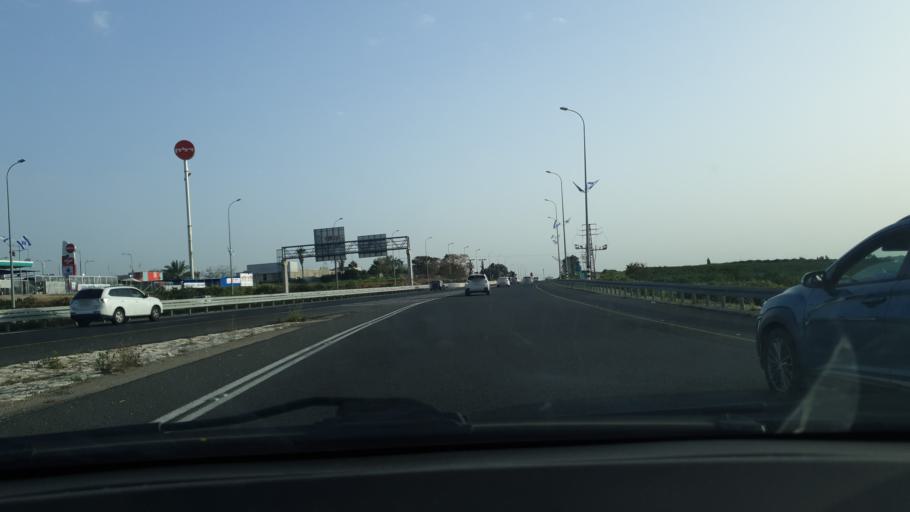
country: IL
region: Central District
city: Even Yehuda
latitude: 32.2522
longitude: 34.8900
